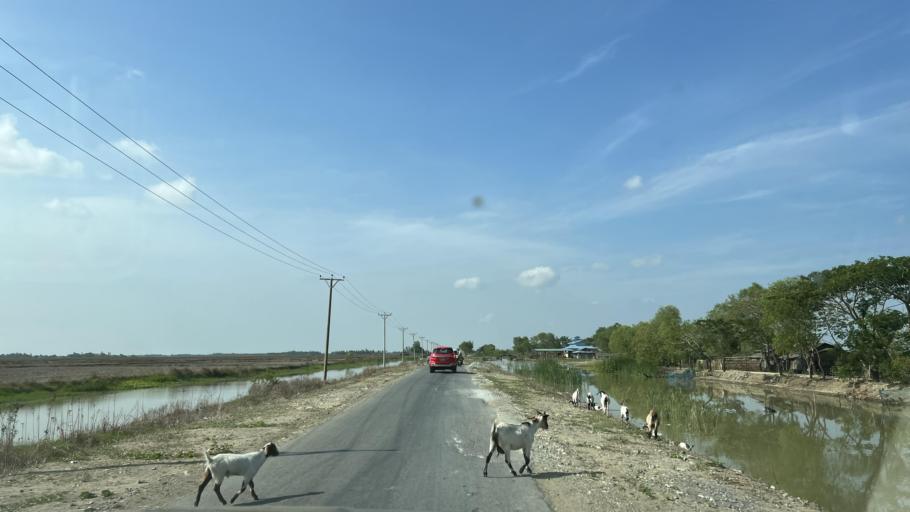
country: MM
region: Ayeyarwady
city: Pyapon
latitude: 16.0478
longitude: 95.6135
